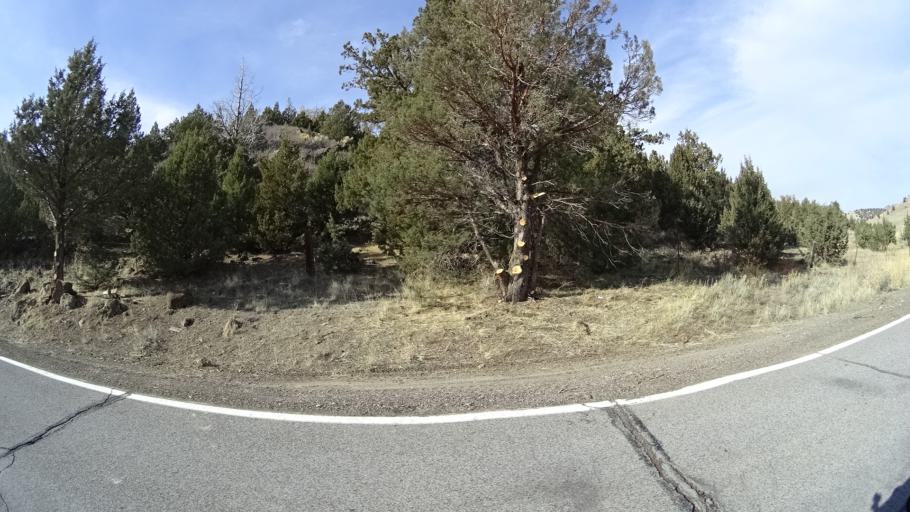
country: US
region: California
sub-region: Siskiyou County
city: Weed
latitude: 41.4862
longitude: -122.4085
